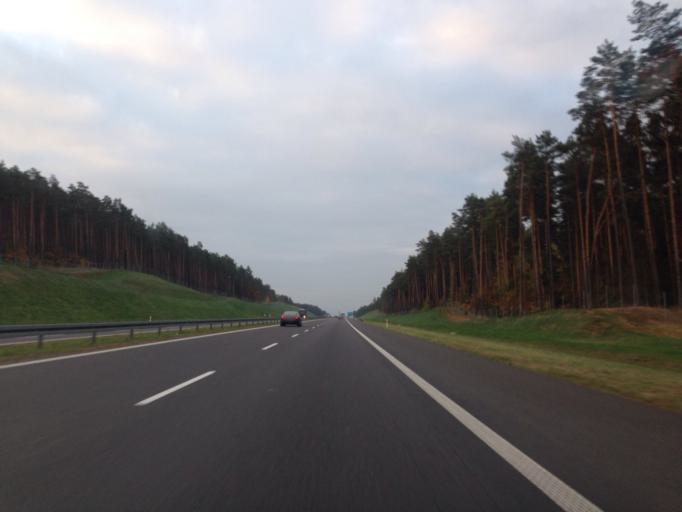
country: PL
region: Kujawsko-Pomorskie
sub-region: Powiat swiecki
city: Warlubie
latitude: 53.4905
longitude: 18.6156
